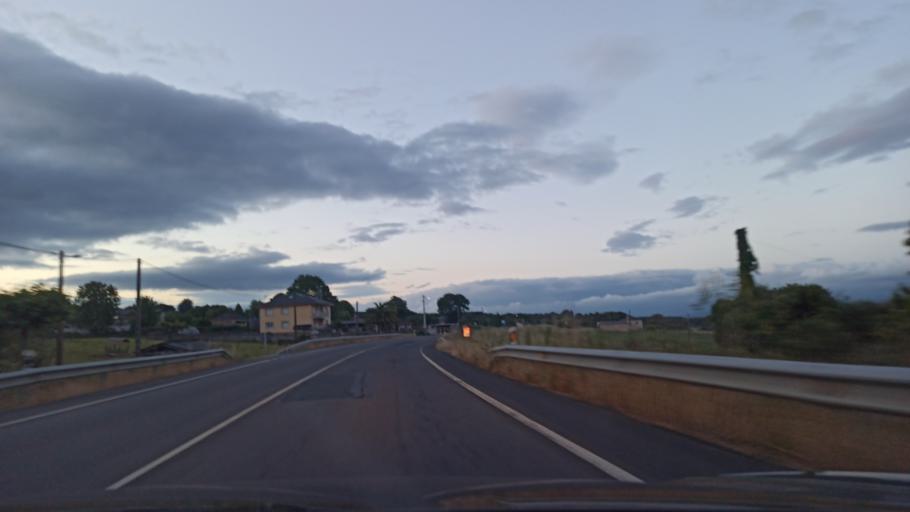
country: ES
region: Galicia
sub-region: Provincia de Lugo
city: Ourol
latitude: 42.9436
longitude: -7.6273
